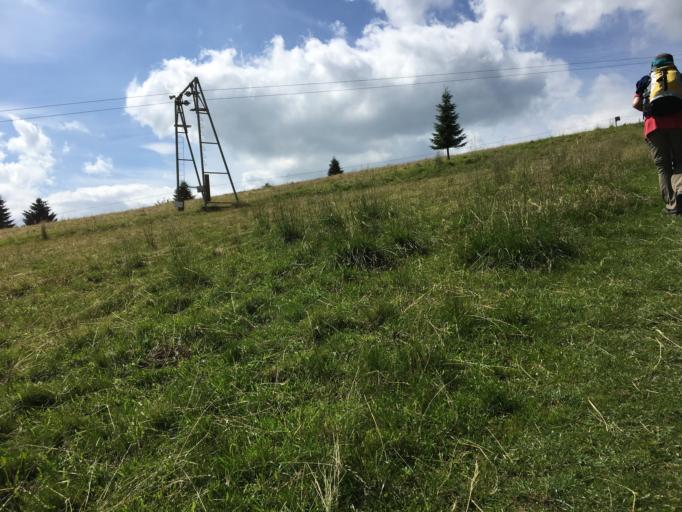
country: DE
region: Hesse
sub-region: Regierungsbezirk Giessen
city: Ulrichstein
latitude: 50.5064
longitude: 9.2263
